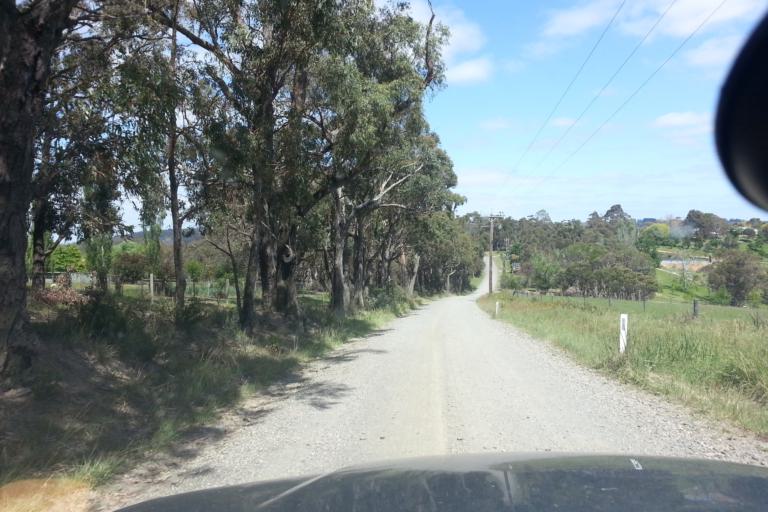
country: AU
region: Victoria
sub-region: Cardinia
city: Beaconsfield Upper
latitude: -37.9840
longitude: 145.3935
